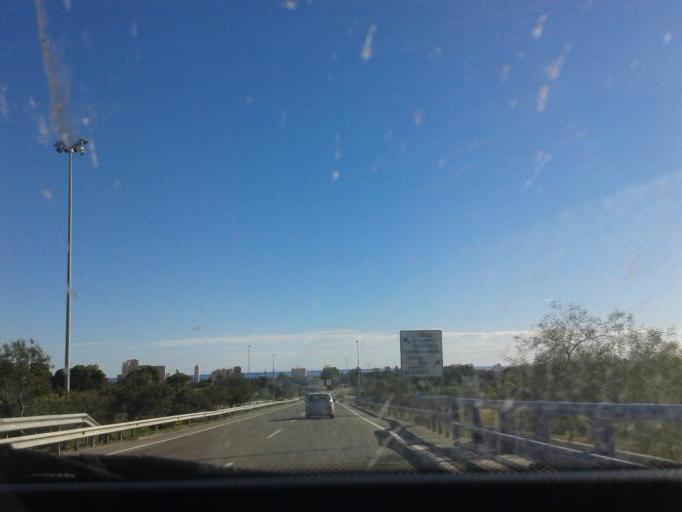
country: ES
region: Valencia
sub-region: Provincia de Alicante
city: Muchamiel
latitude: 38.4191
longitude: -0.4255
